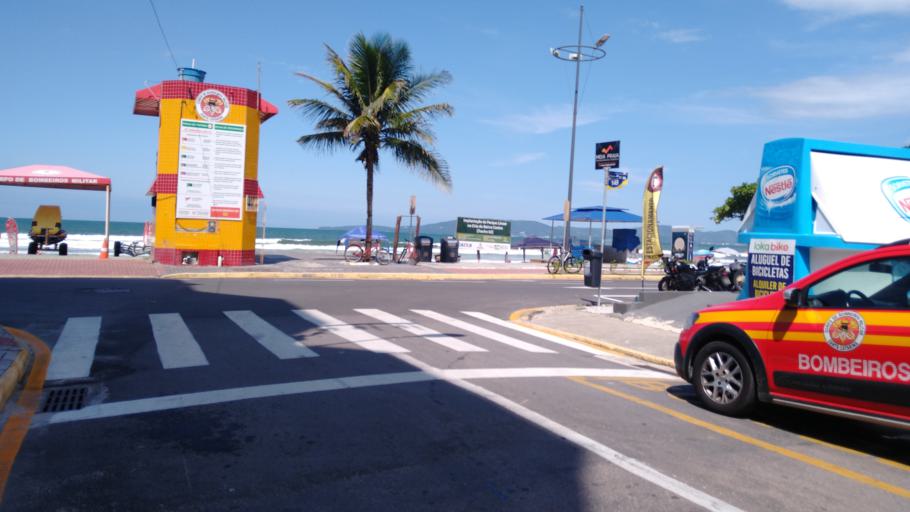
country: BR
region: Santa Catarina
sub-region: Itapema
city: Itapema
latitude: -27.1014
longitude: -48.6141
